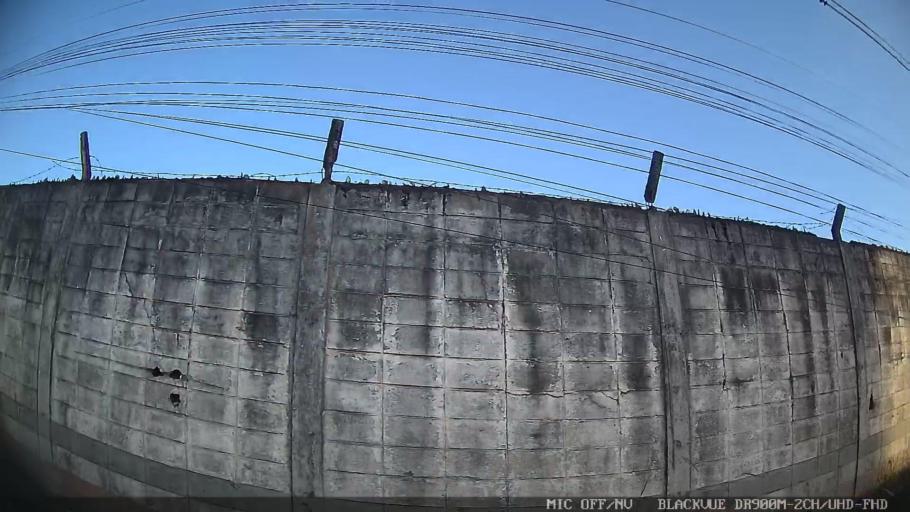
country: BR
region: Sao Paulo
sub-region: Guaruja
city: Guaruja
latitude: -23.9733
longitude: -46.2669
